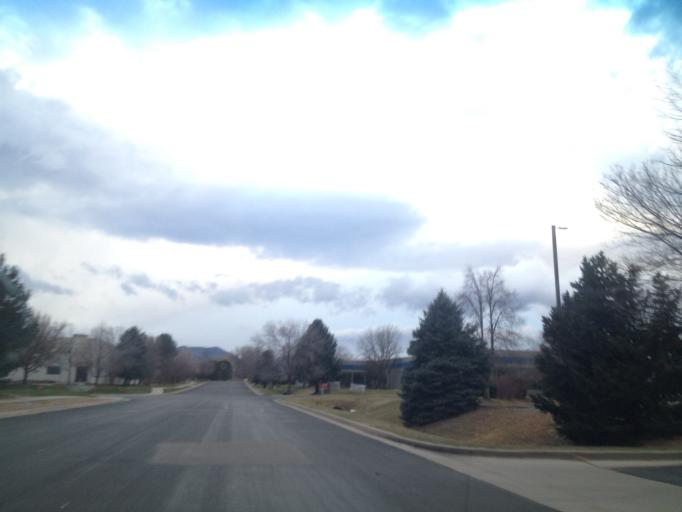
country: US
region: Colorado
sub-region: Boulder County
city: Louisville
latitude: 39.9650
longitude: -105.1215
